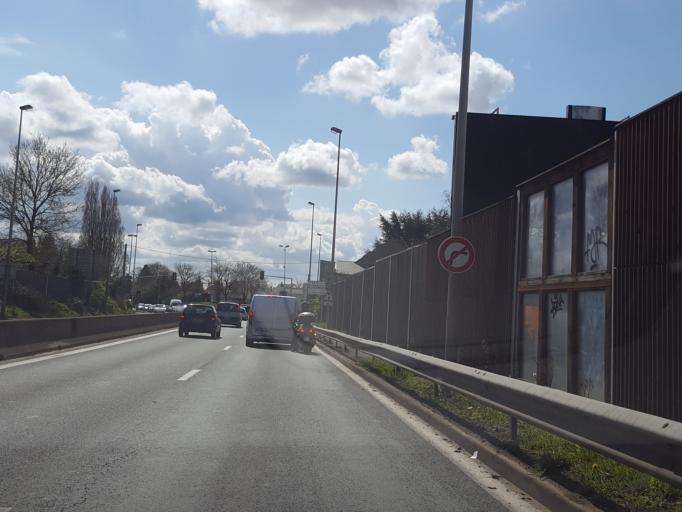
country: FR
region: Centre
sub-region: Departement du Loiret
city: Saint-Jean-de-la-Ruelle
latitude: 47.9125
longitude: 1.8671
